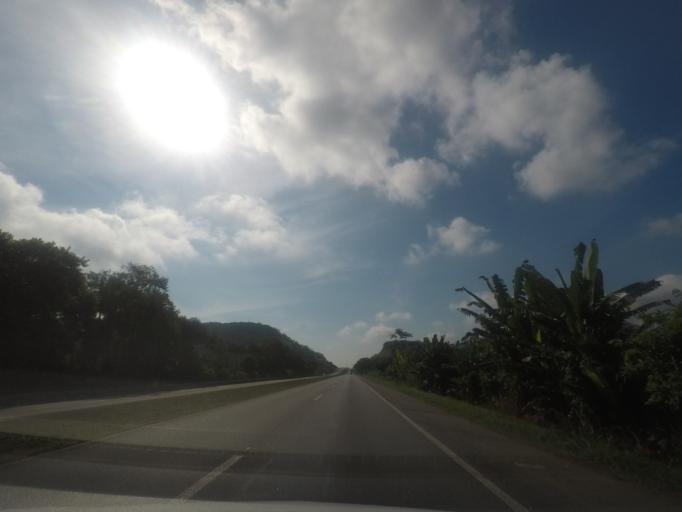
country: BR
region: Parana
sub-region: Antonina
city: Antonina
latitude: -25.5359
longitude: -48.7639
